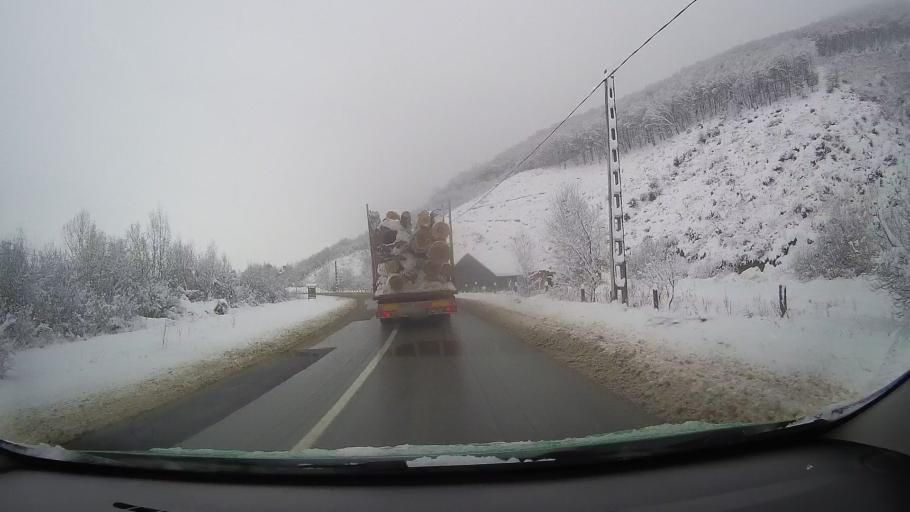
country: RO
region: Sibiu
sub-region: Comuna Orlat
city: Orlat
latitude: 45.7596
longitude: 23.9408
